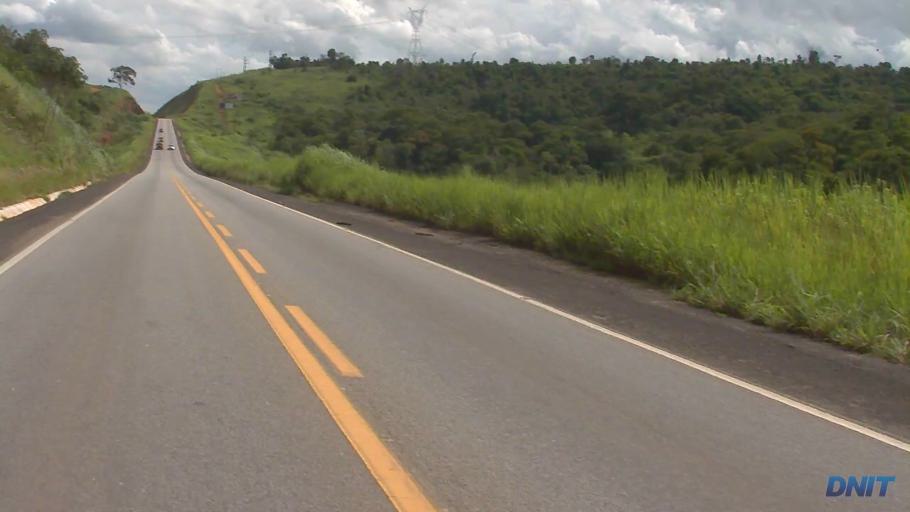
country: BR
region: Minas Gerais
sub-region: Ipaba
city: Ipaba
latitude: -19.4122
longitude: -42.4899
